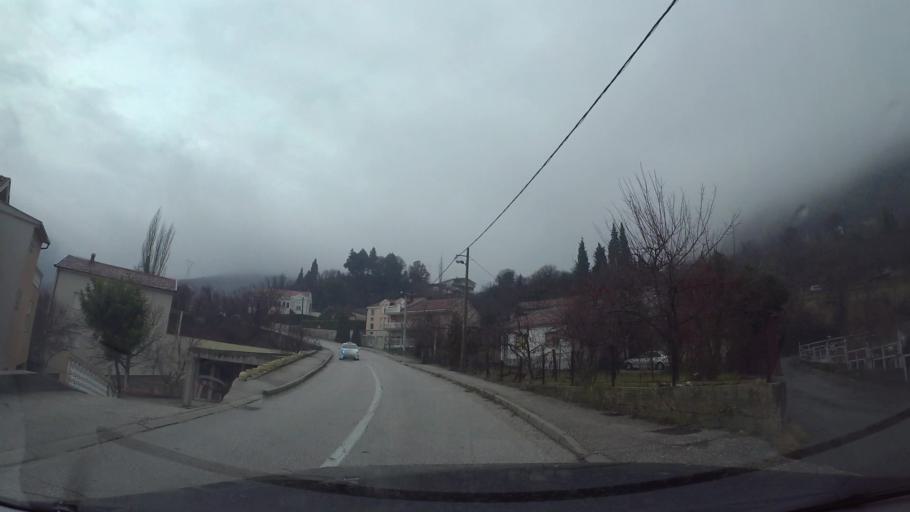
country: BA
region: Federation of Bosnia and Herzegovina
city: Cim
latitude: 43.3562
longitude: 17.7738
